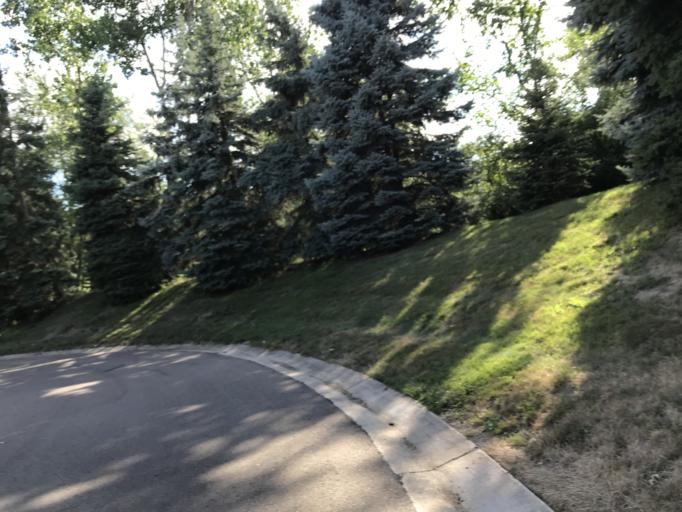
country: US
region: Michigan
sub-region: Oakland County
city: Farmington Hills
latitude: 42.4798
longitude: -83.3417
